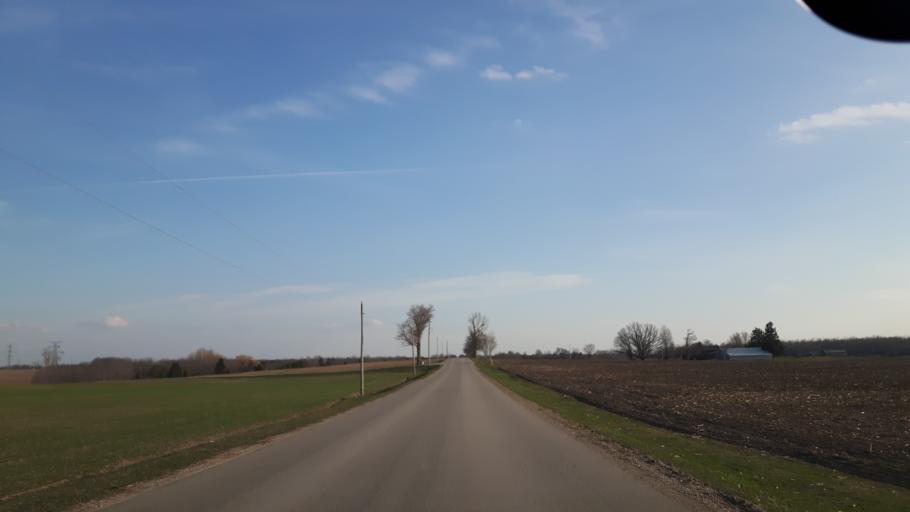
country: CA
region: Ontario
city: Goderich
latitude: 43.6928
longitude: -81.6645
